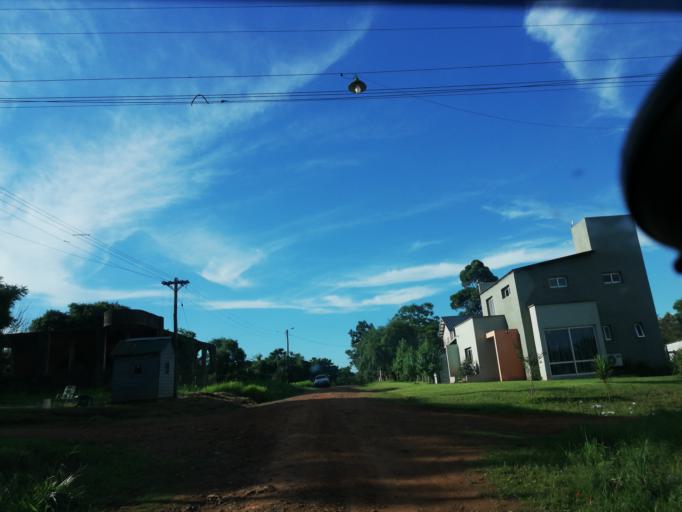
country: AR
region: Misiones
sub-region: Departamento de Capital
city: Posadas
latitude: -27.4003
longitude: -55.9602
